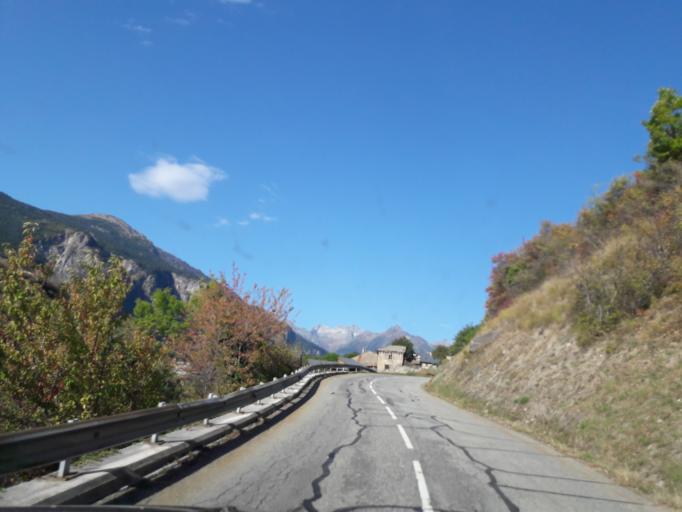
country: FR
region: Rhone-Alpes
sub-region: Departement de la Savoie
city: Saint-Jean-de-Maurienne
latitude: 45.3047
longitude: 6.3649
